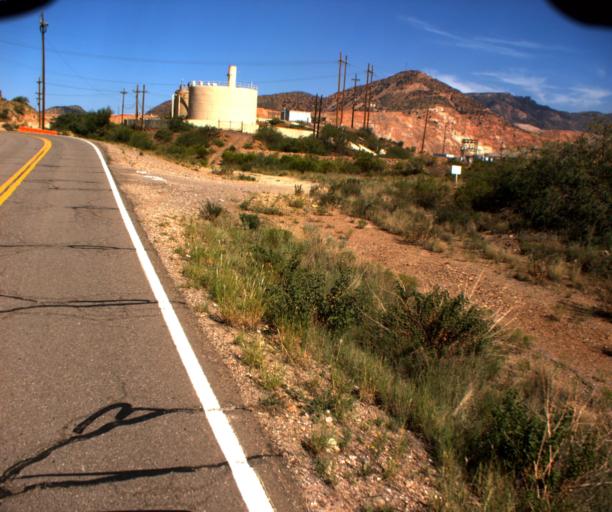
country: US
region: Arizona
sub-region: Greenlee County
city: Morenci
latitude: 33.0724
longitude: -109.3673
